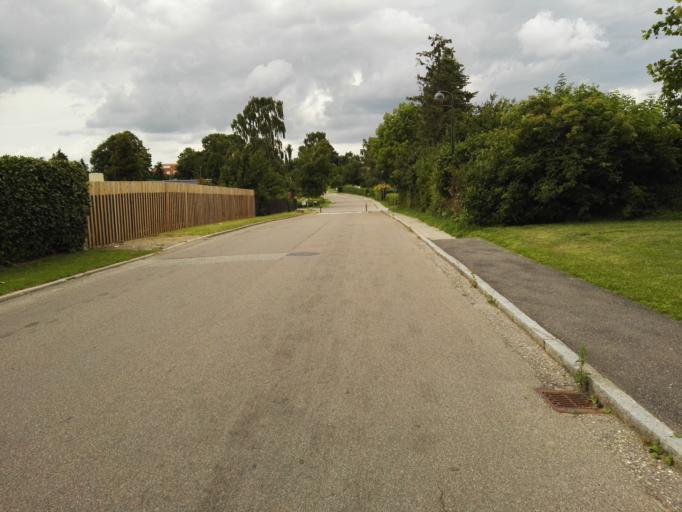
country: DK
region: Capital Region
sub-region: Egedal Kommune
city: Olstykke
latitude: 55.7805
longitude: 12.1718
